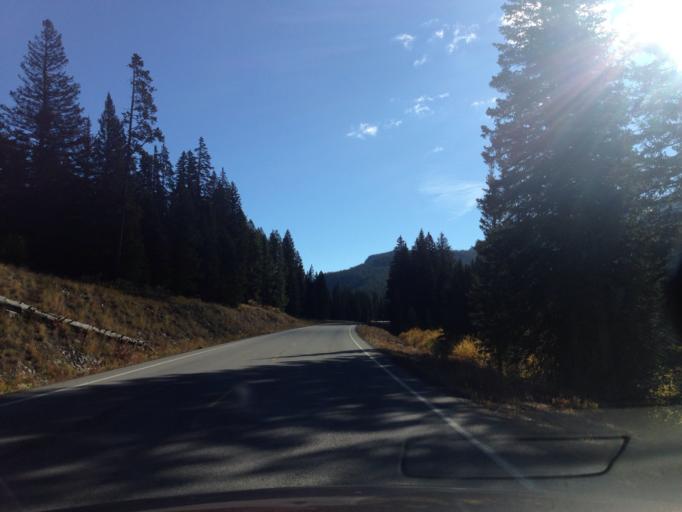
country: US
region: Montana
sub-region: Stillwater County
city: Absarokee
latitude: 45.0183
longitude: -109.9466
